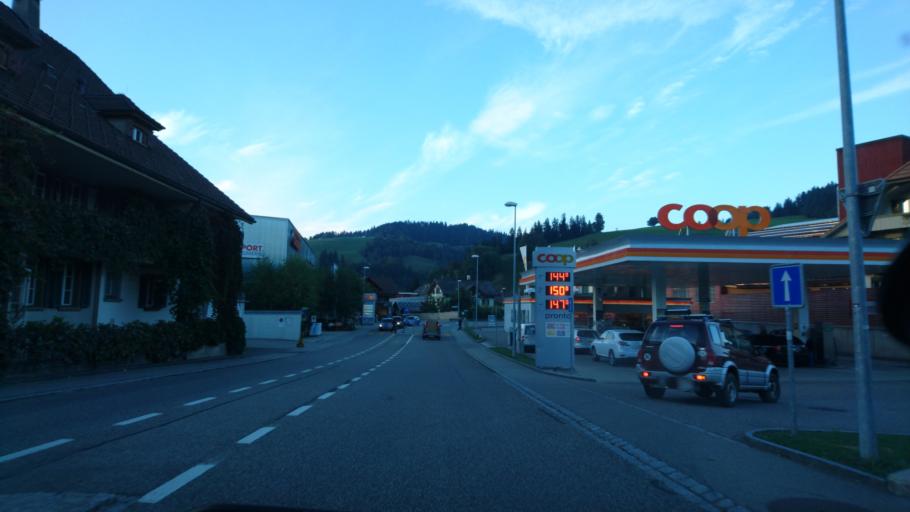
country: CH
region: Bern
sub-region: Emmental District
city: Langnau
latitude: 46.9400
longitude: 7.7791
